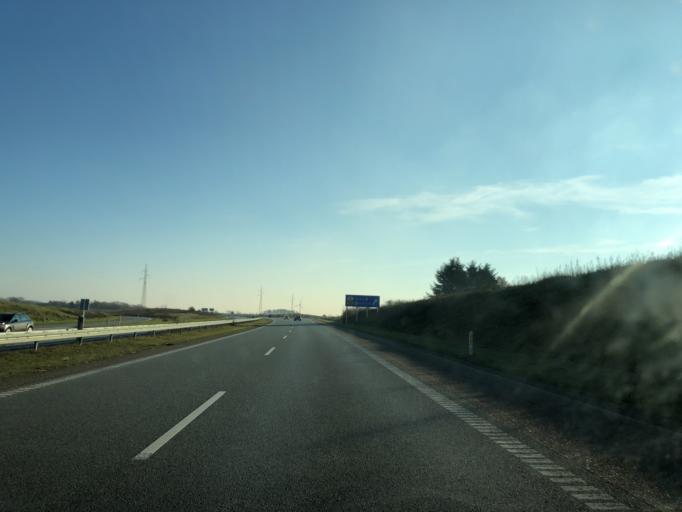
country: DK
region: South Denmark
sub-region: Vejle Kommune
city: Give
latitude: 55.8467
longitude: 9.2703
